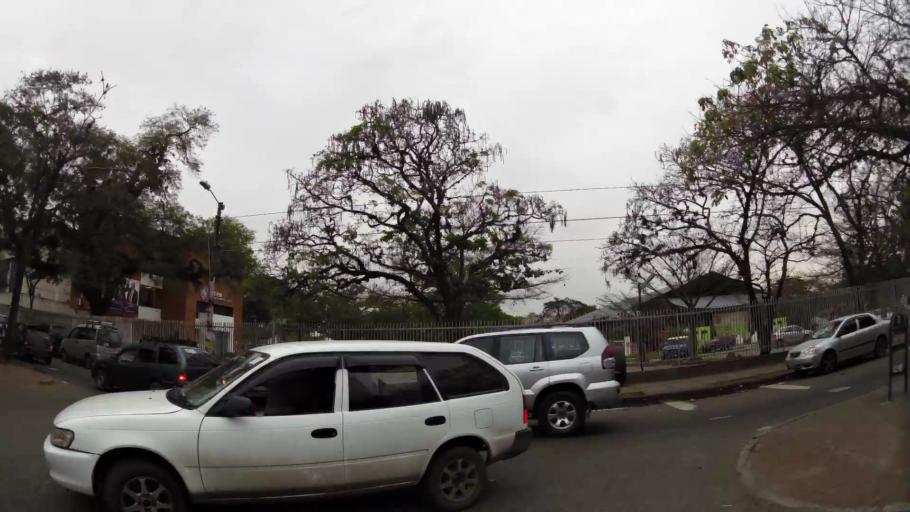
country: BO
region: Santa Cruz
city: Santa Cruz de la Sierra
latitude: -17.7797
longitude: -63.1921
